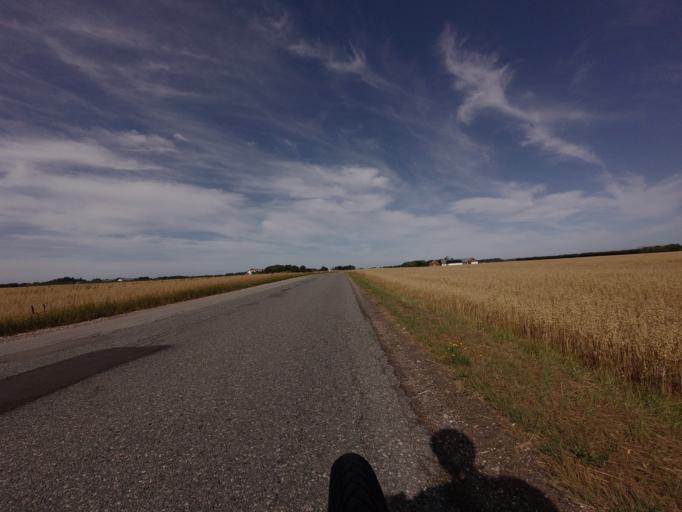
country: DK
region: North Denmark
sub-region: Hjorring Kommune
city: Vra
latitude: 57.4148
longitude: 9.8703
